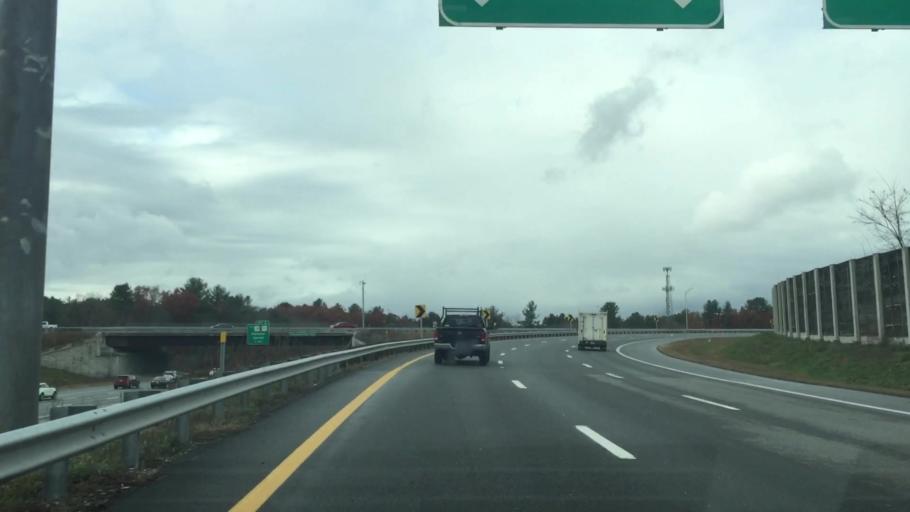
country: US
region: New Hampshire
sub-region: Rockingham County
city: Salem
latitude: 42.7605
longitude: -71.2318
